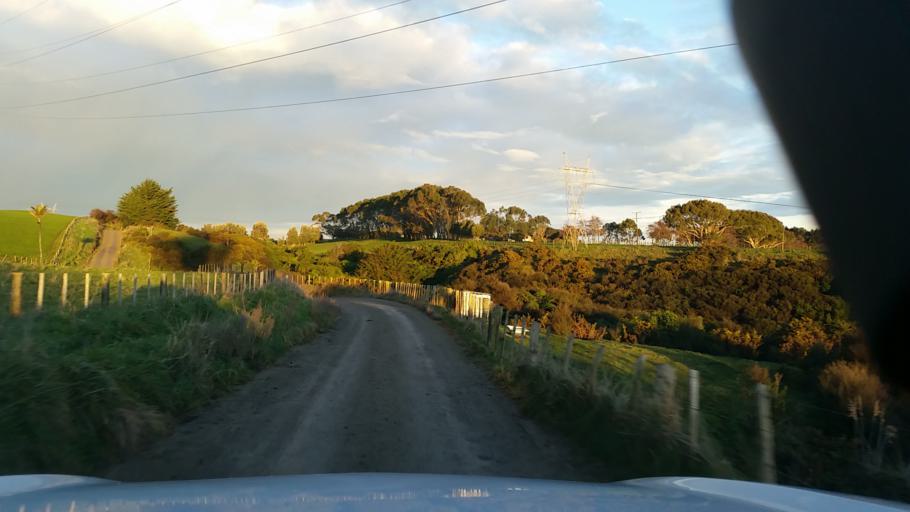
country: NZ
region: Manawatu-Wanganui
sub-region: Wanganui District
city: Wanganui
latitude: -39.7991
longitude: 174.7997
